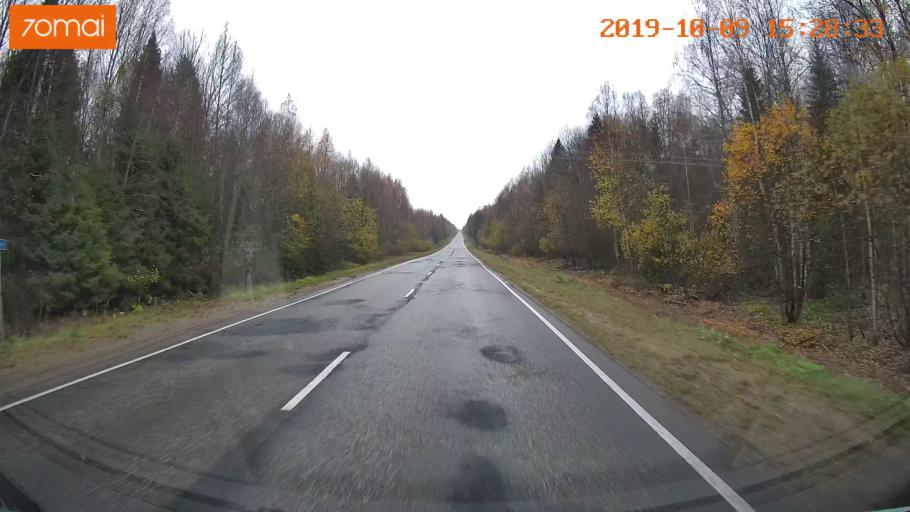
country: RU
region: Kostroma
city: Susanino
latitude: 58.0017
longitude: 41.3579
